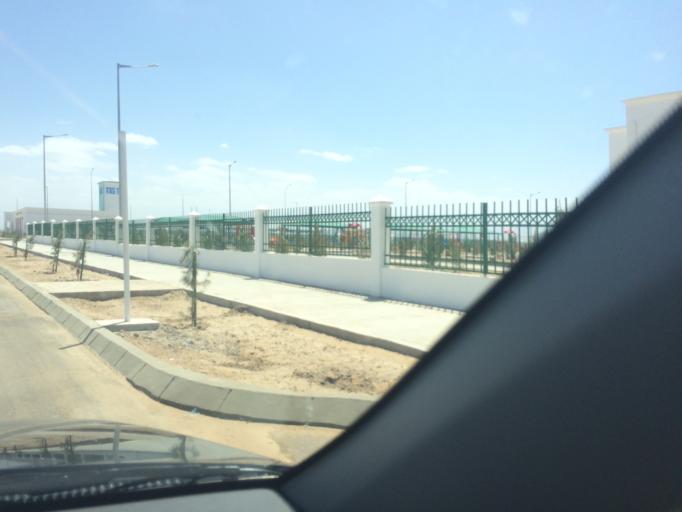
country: TM
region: Ahal
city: Abadan
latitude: 38.0958
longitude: 58.2939
